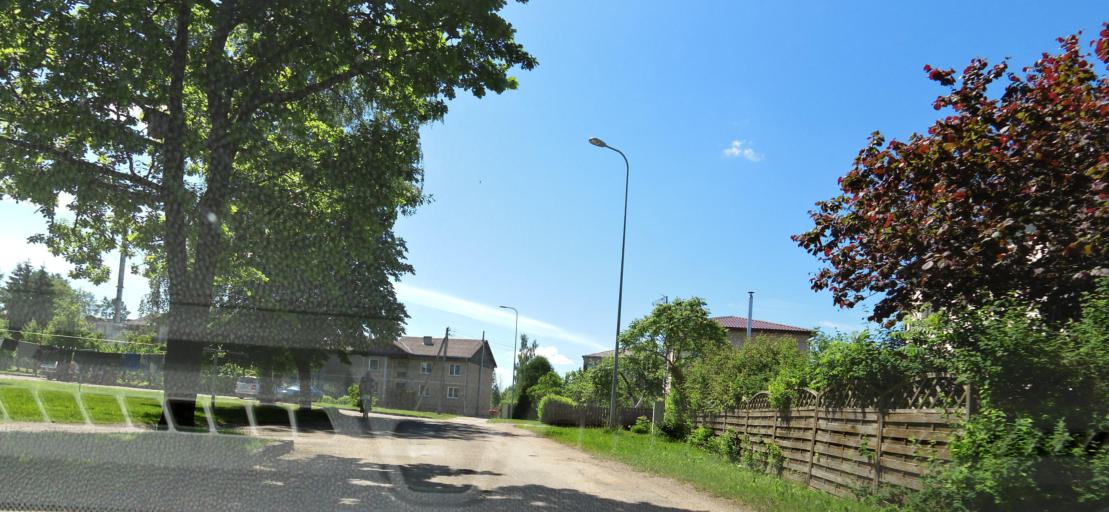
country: LT
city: Moletai
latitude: 55.0770
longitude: 25.2556
